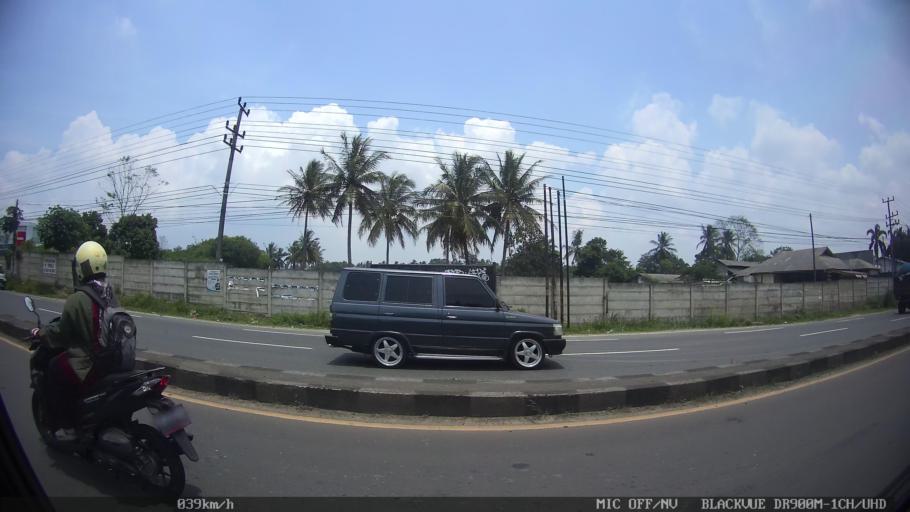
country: ID
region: Lampung
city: Natar
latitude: -5.3498
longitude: 105.2178
